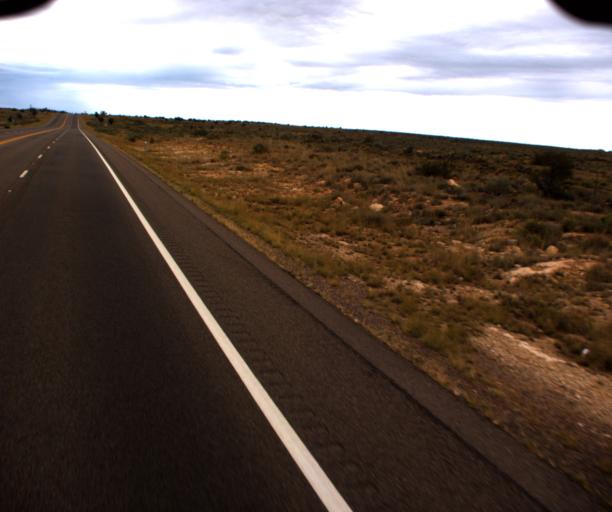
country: US
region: Arizona
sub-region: Navajo County
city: Snowflake
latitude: 34.5851
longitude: -110.0853
